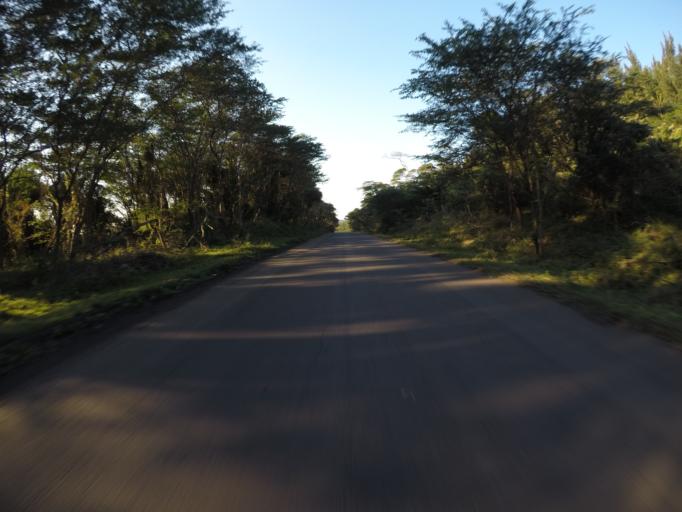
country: ZA
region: KwaZulu-Natal
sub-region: uThungulu District Municipality
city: KwaMbonambi
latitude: -28.6971
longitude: 32.2083
